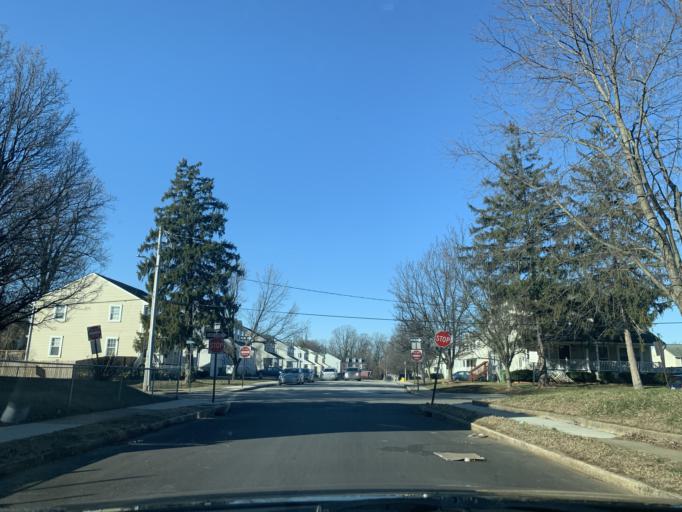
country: US
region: Maryland
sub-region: Baltimore County
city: Lochearn
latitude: 39.3350
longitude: -76.6867
